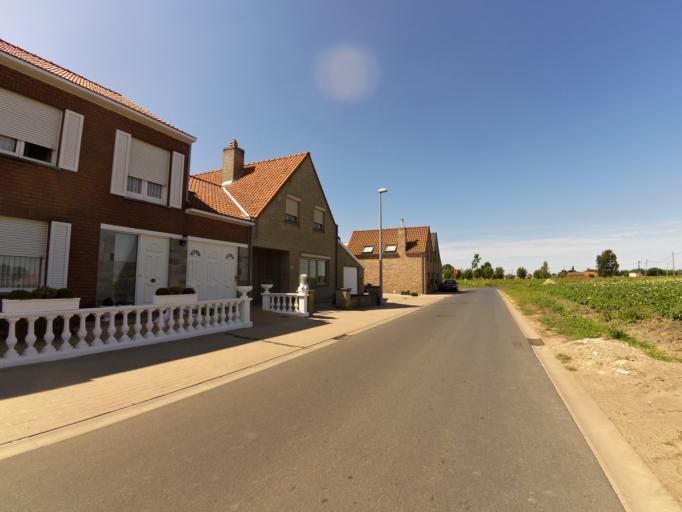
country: BE
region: Flanders
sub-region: Provincie West-Vlaanderen
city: Ichtegem
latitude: 51.1355
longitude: 3.0352
